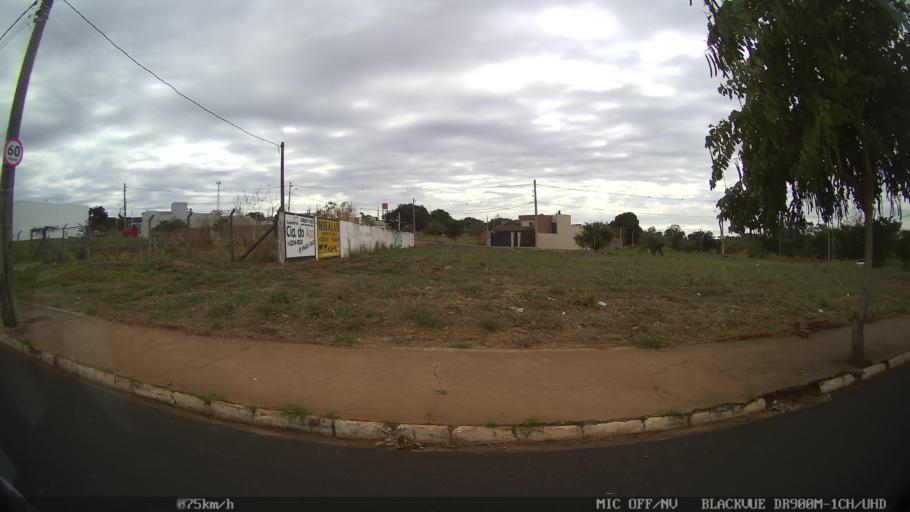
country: BR
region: Sao Paulo
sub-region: Sao Jose Do Rio Preto
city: Sao Jose do Rio Preto
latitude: -20.8170
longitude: -49.4852
